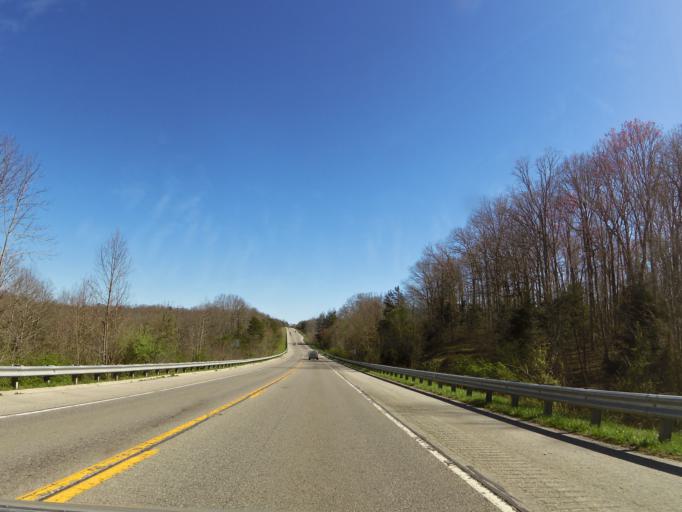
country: US
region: Kentucky
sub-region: McCreary County
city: Stearns
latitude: 36.6849
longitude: -84.4518
